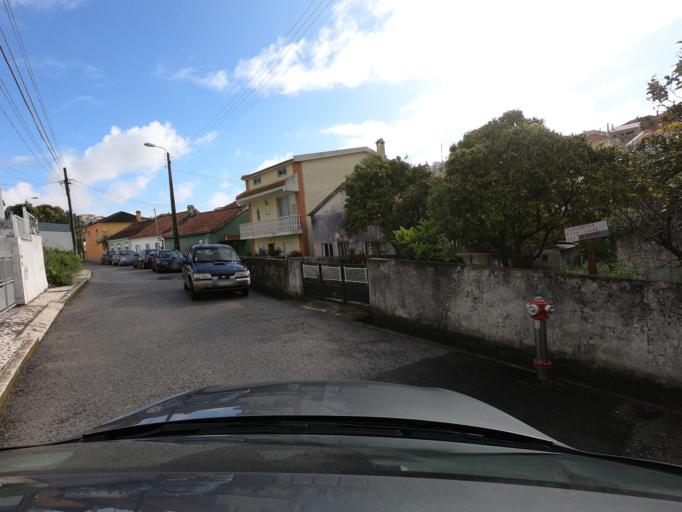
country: PT
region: Lisbon
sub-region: Oeiras
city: Porto Salvo
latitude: 38.7208
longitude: -9.3112
